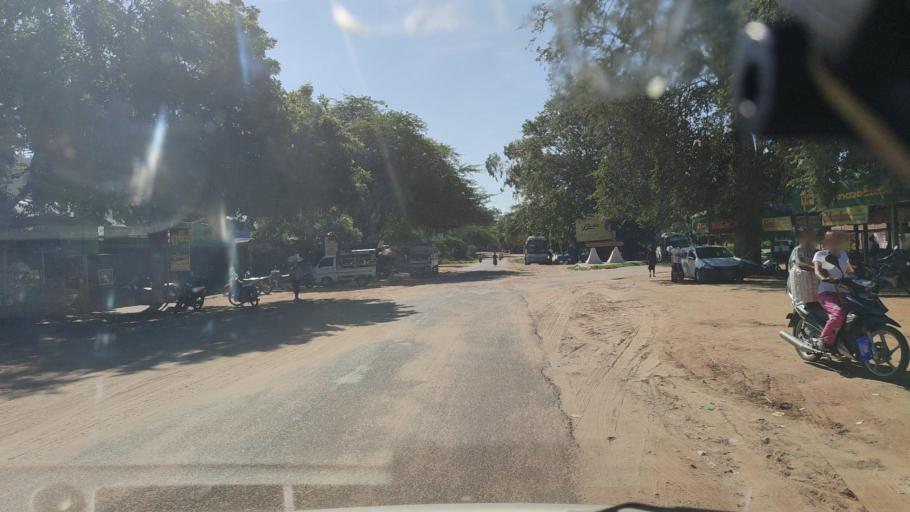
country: MM
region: Magway
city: Taungdwingyi
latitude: 19.9570
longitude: 95.2490
